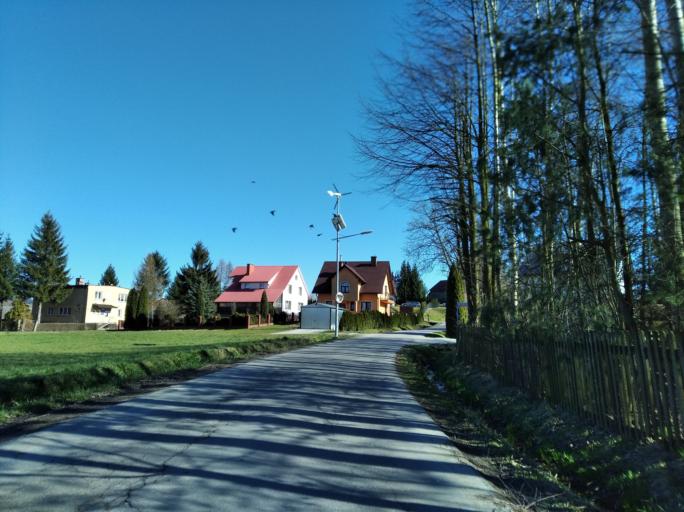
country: PL
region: Subcarpathian Voivodeship
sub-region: Powiat strzyzowski
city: Wisniowa
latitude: 49.9134
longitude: 21.7088
